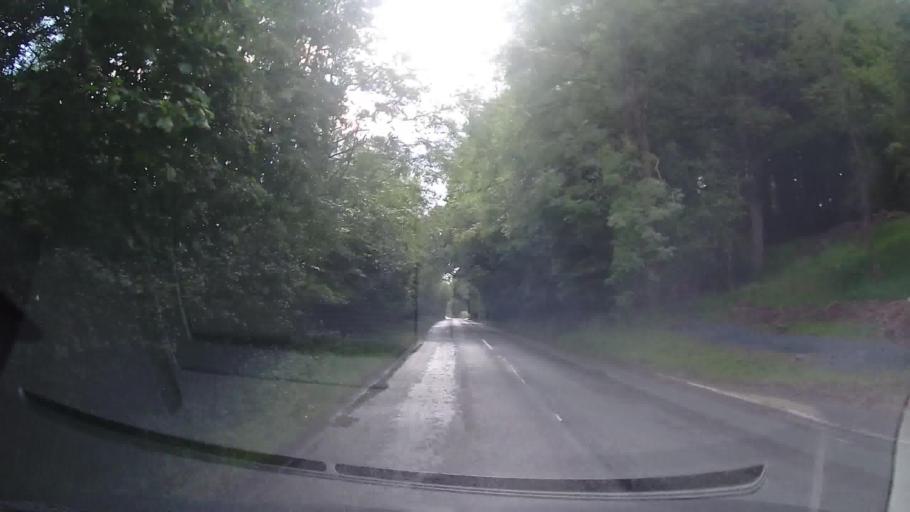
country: GB
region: England
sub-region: Telford and Wrekin
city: Ironbridge
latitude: 52.6383
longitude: -2.5158
